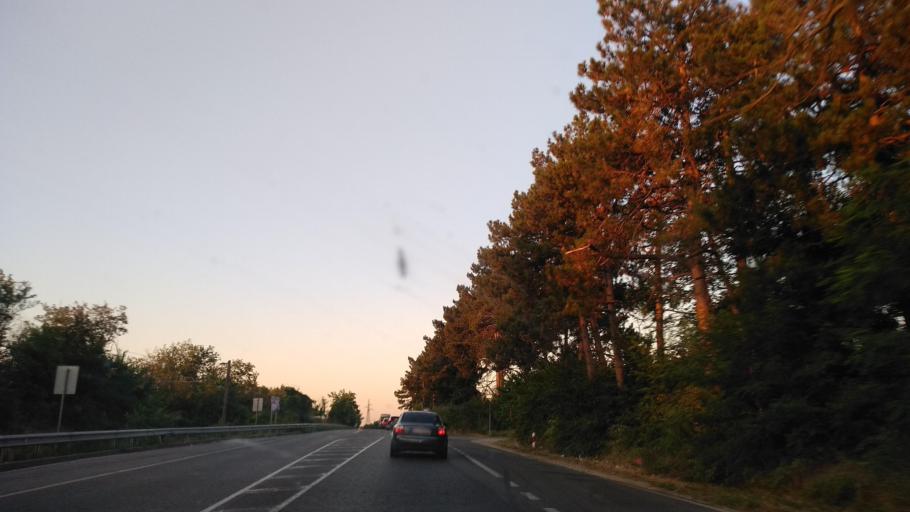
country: RO
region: Giurgiu
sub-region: Comuna Slobozia
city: Slobozia
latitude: 43.7744
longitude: 25.8983
